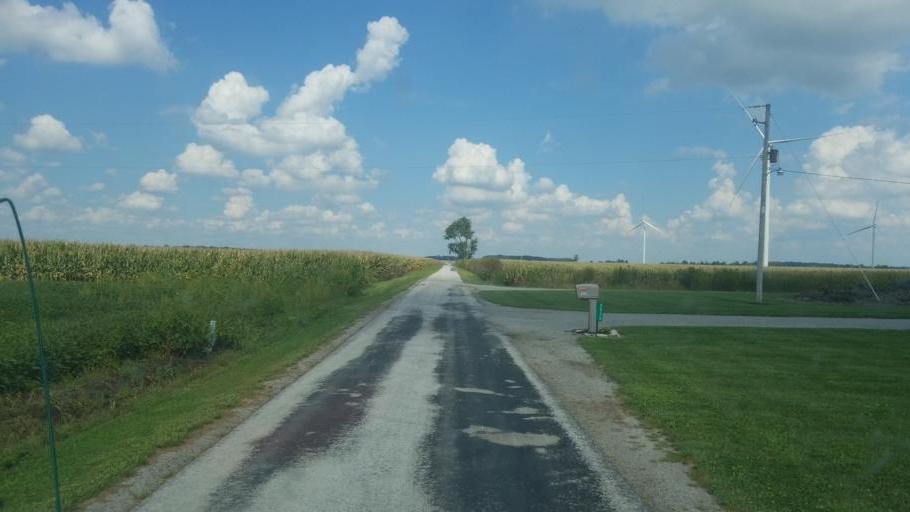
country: US
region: Ohio
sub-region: Hardin County
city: Ada
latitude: 40.7831
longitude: -83.7479
